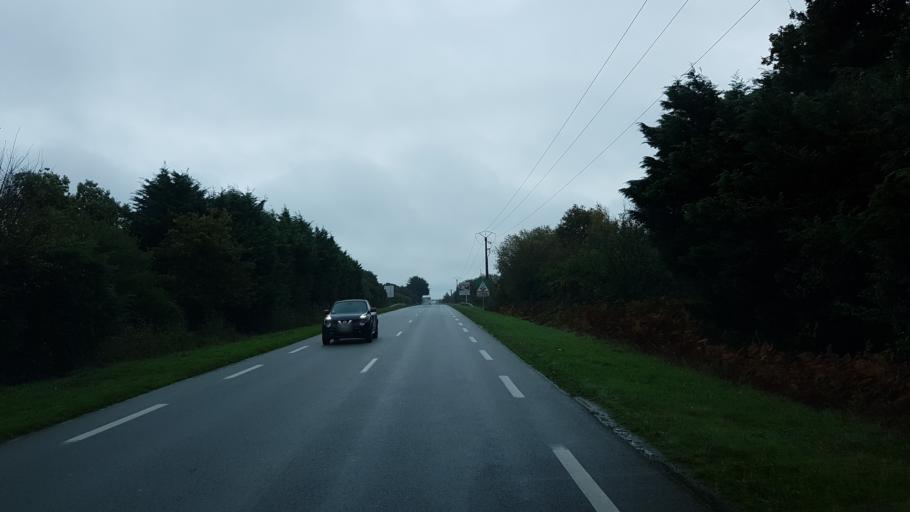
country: FR
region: Brittany
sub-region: Departement du Morbihan
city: Sarzeau
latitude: 47.5250
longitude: -2.7901
